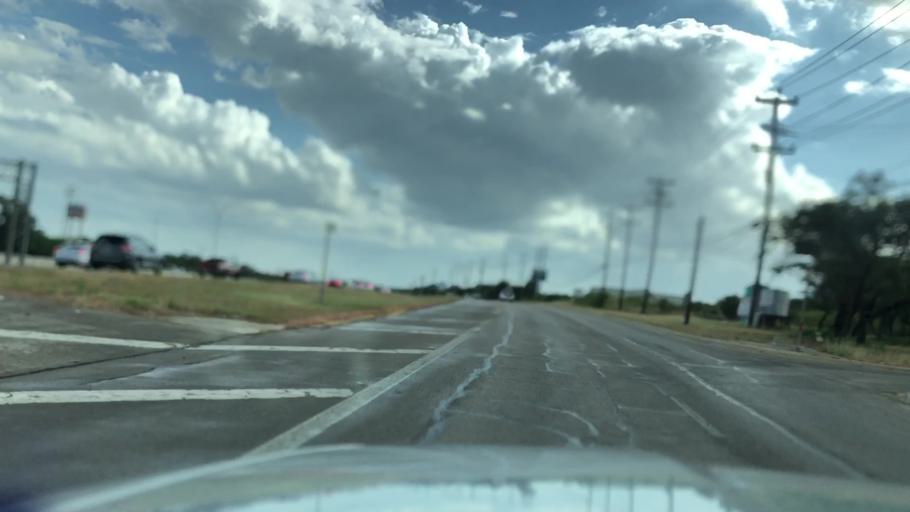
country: US
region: Texas
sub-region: Bexar County
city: Helotes
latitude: 29.5858
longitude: -98.6373
